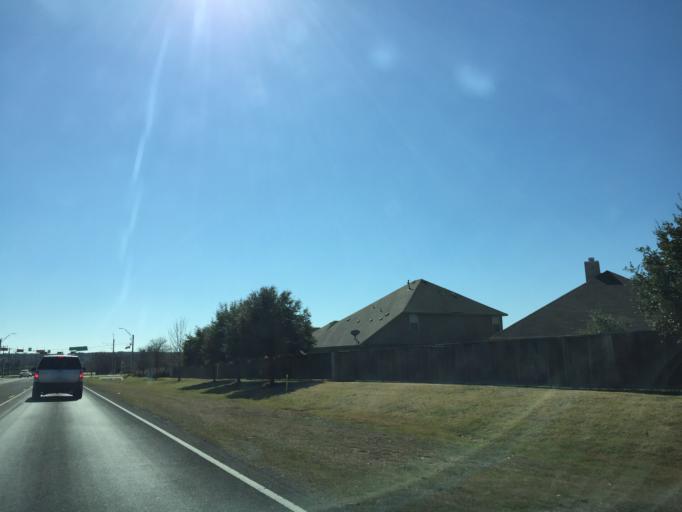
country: US
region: Texas
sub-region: Williamson County
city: Hutto
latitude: 30.5377
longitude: -97.6141
